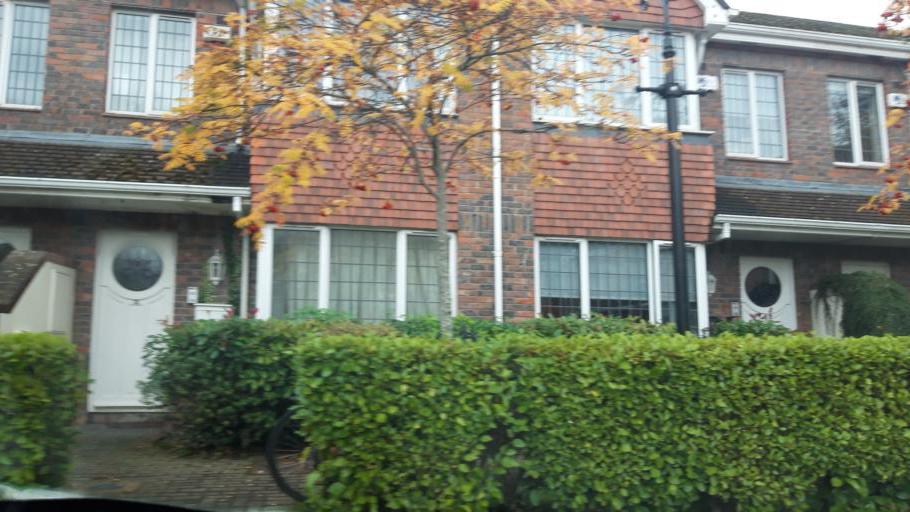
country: IE
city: Milltown
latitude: 53.3184
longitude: -6.2470
